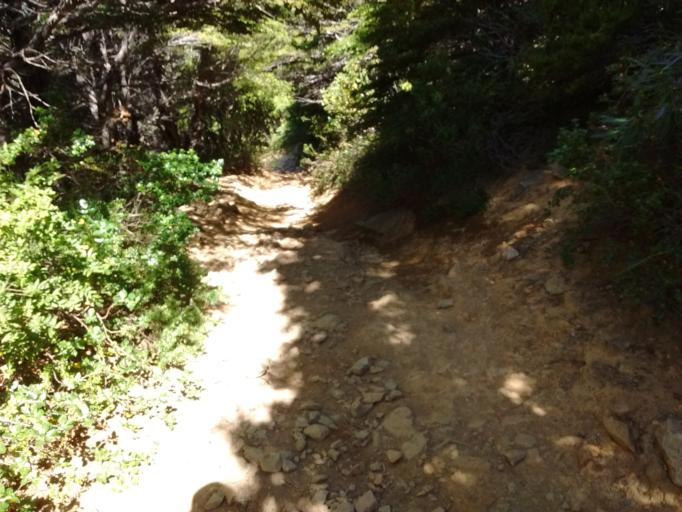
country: AR
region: Rio Negro
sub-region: Departamento de Bariloche
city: San Carlos de Bariloche
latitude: -41.0725
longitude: -71.5788
